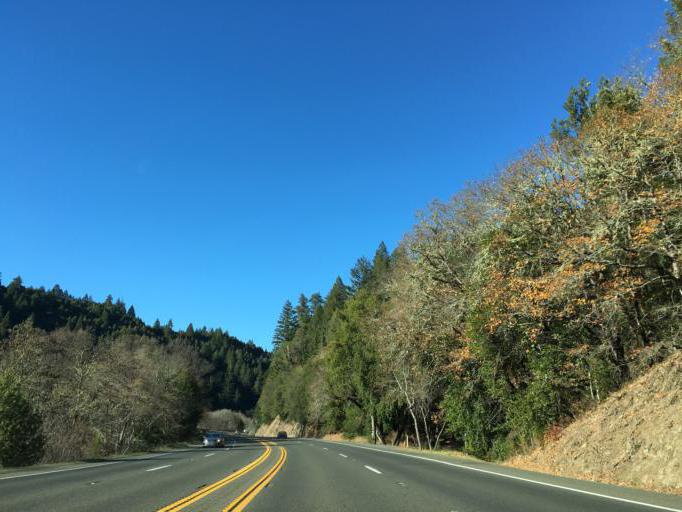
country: US
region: California
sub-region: Mendocino County
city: Brooktrails
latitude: 39.5269
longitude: -123.4011
